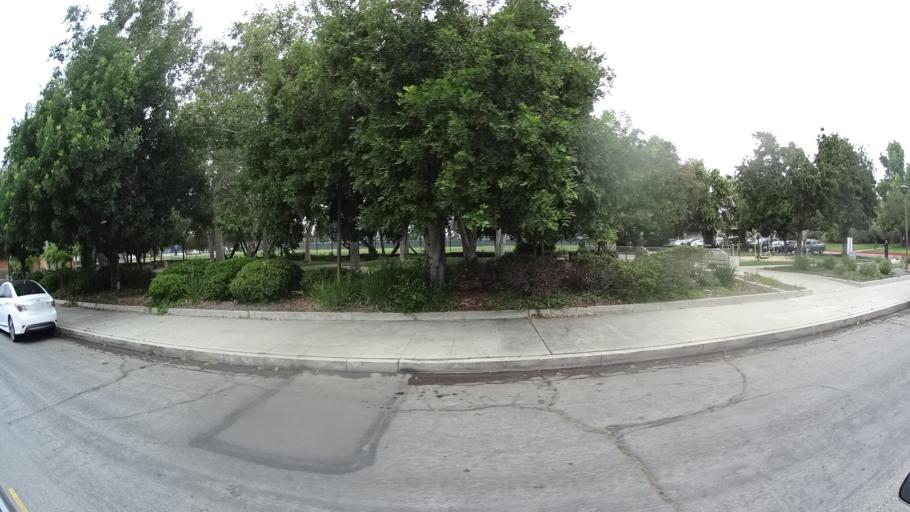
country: US
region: California
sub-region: Los Angeles County
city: Burbank
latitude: 34.1863
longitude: -118.3447
